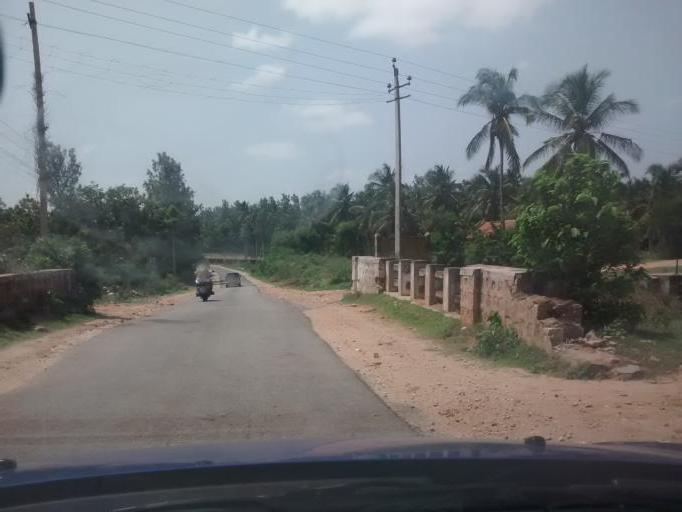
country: IN
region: Karnataka
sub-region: Hassan
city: Konanur
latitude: 12.5680
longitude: 76.2378
